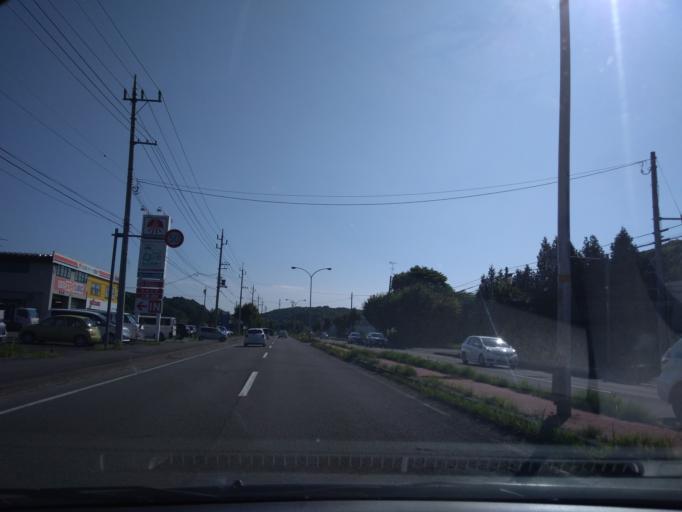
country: JP
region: Hokkaido
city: Kitahiroshima
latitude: 42.9811
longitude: 141.5513
